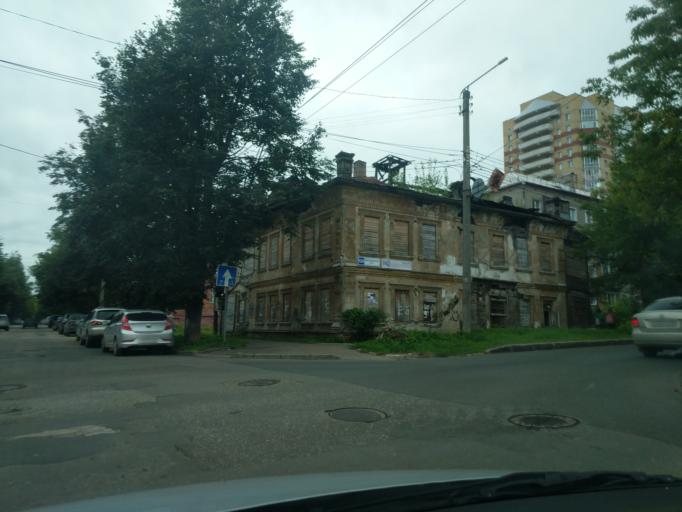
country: RU
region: Kirov
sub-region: Kirovo-Chepetskiy Rayon
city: Kirov
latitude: 58.5962
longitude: 49.6728
